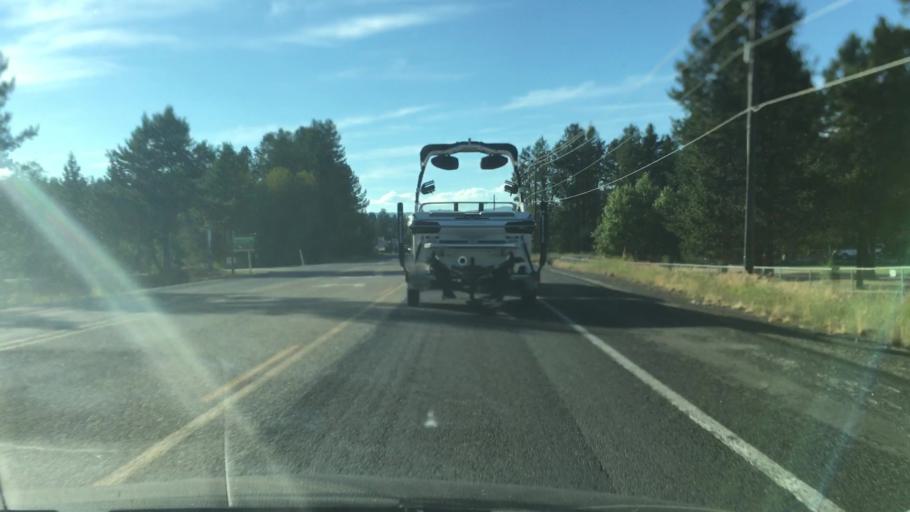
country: US
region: Idaho
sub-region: Valley County
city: Cascade
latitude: 44.5024
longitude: -116.0259
